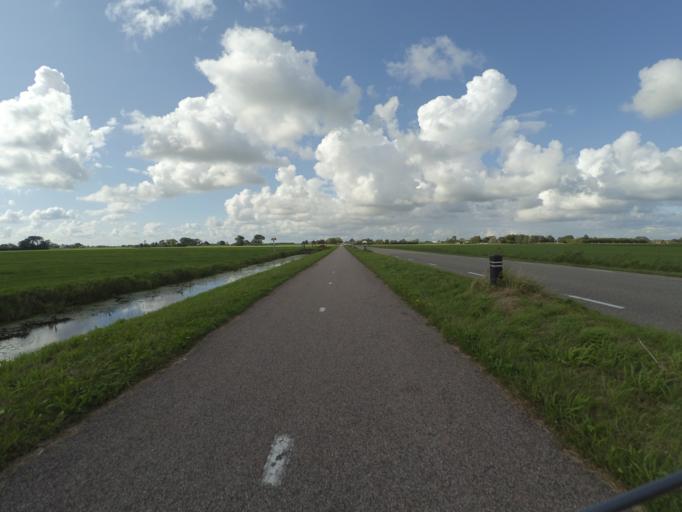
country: NL
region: North Holland
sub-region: Gemeente Schagen
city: Schagen
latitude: 52.8113
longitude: 4.7946
